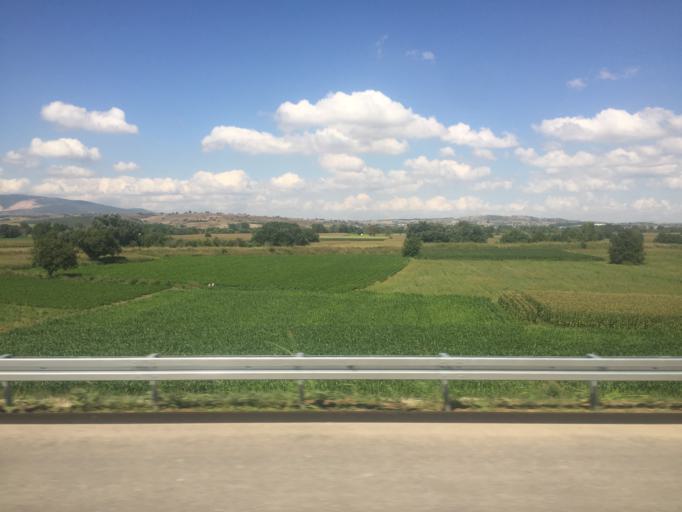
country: TR
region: Balikesir
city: Gobel
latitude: 40.0026
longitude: 28.1938
